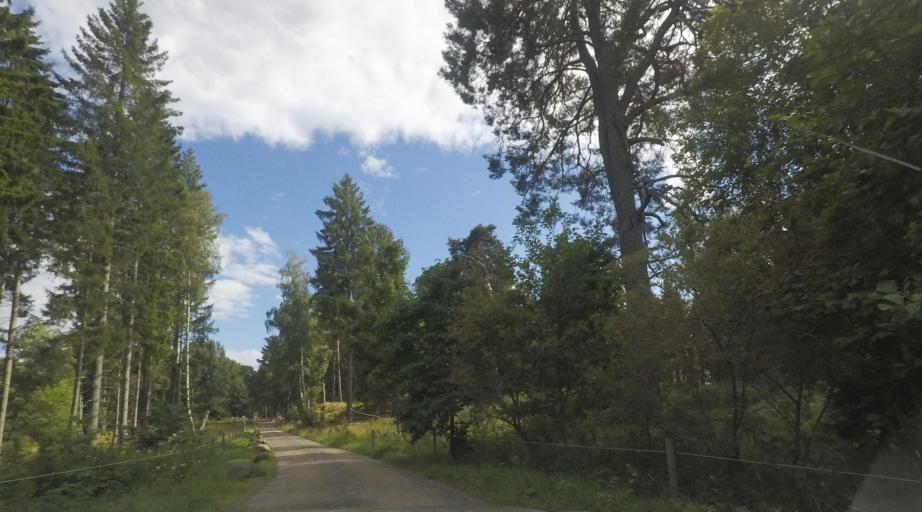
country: SE
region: Stockholm
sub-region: Sodertalje Kommun
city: Pershagen
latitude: 59.1050
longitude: 17.6784
